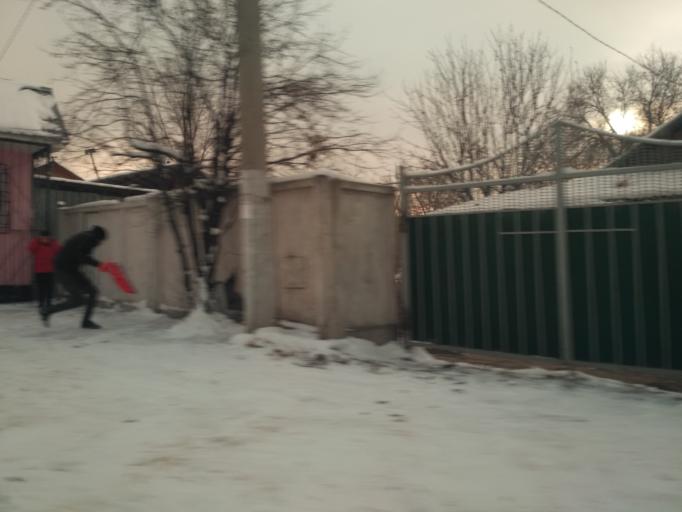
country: KZ
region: Almaty Qalasy
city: Almaty
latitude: 43.2143
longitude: 76.7869
